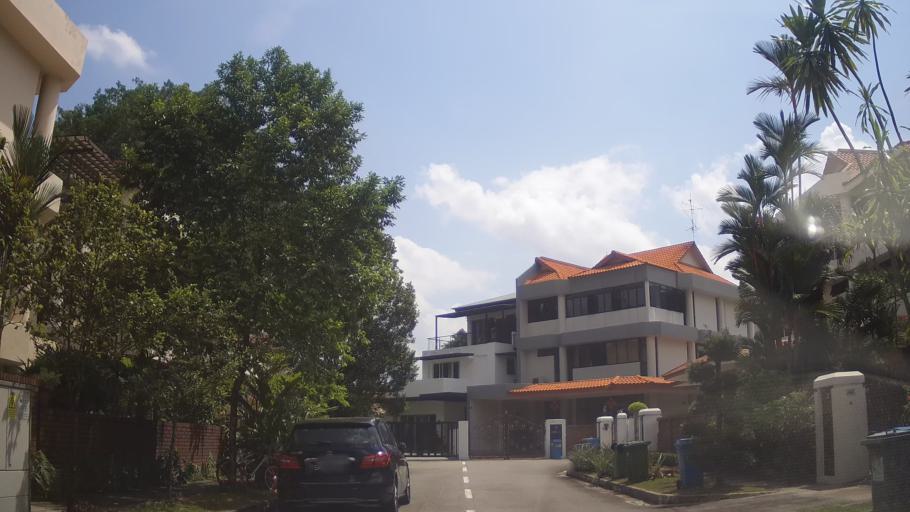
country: MY
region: Johor
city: Johor Bahru
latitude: 1.3691
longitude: 103.7685
